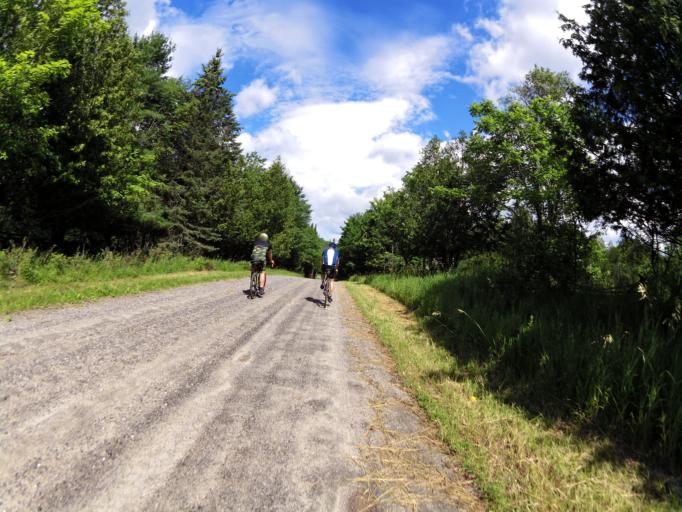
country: CA
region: Ontario
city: Perth
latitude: 45.0763
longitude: -76.4623
